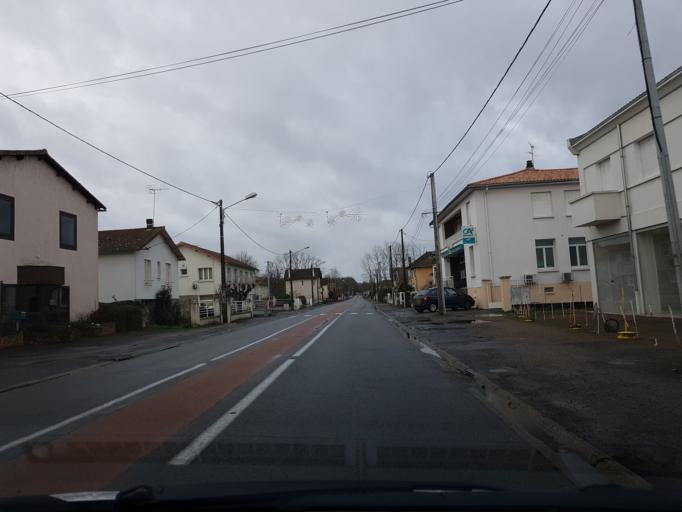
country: FR
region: Poitou-Charentes
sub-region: Departement de la Charente
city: Chabanais
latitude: 45.8737
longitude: 0.7143
